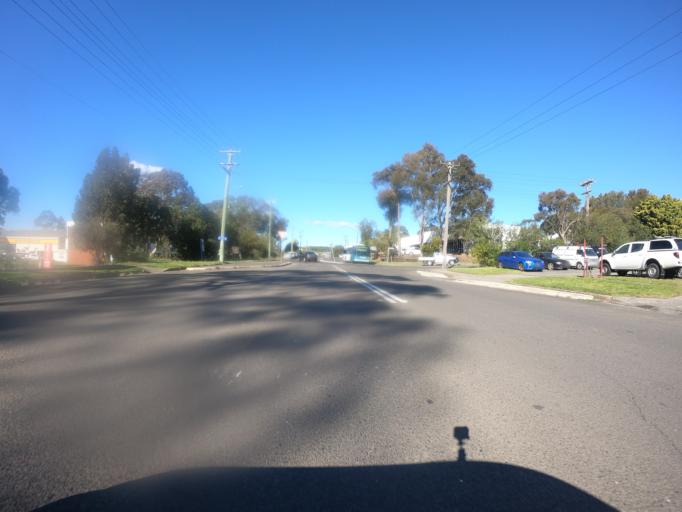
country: AU
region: New South Wales
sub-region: Wollongong
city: Cordeaux Heights
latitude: -34.4564
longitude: 150.8482
